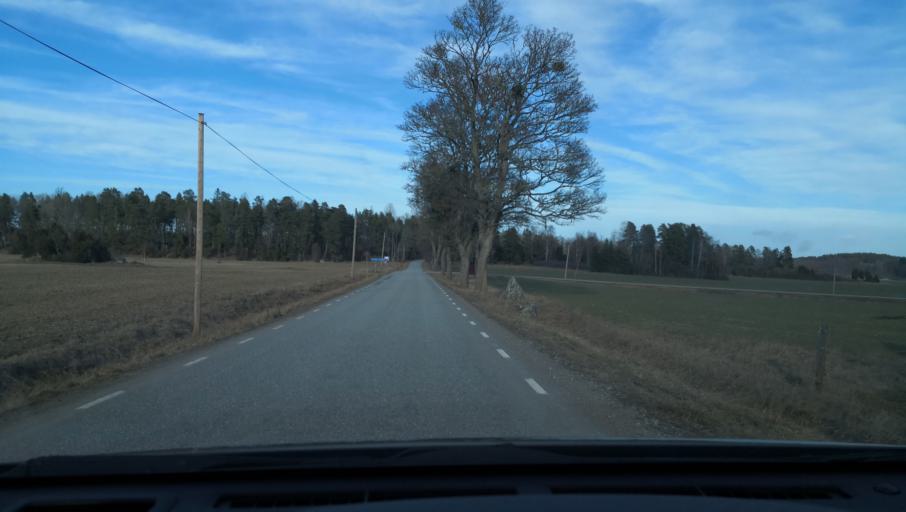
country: SE
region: Uppsala
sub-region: Enkopings Kommun
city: Grillby
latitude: 59.5482
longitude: 17.2148
